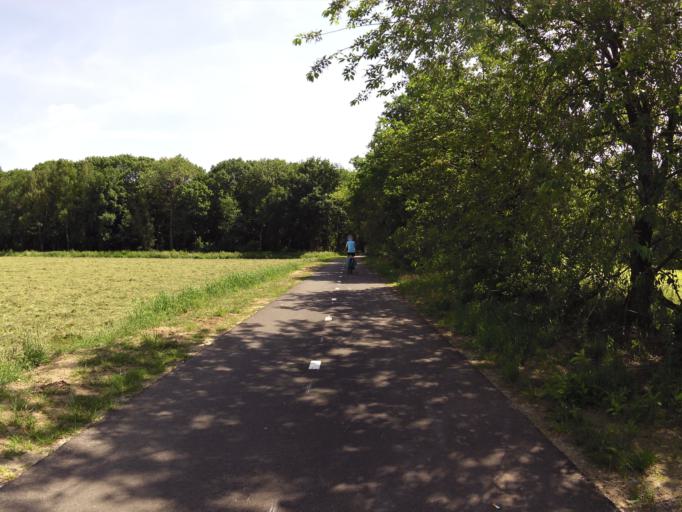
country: NL
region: North Brabant
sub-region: Gemeente Son en Breugel
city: Son
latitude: 51.5240
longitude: 5.4641
